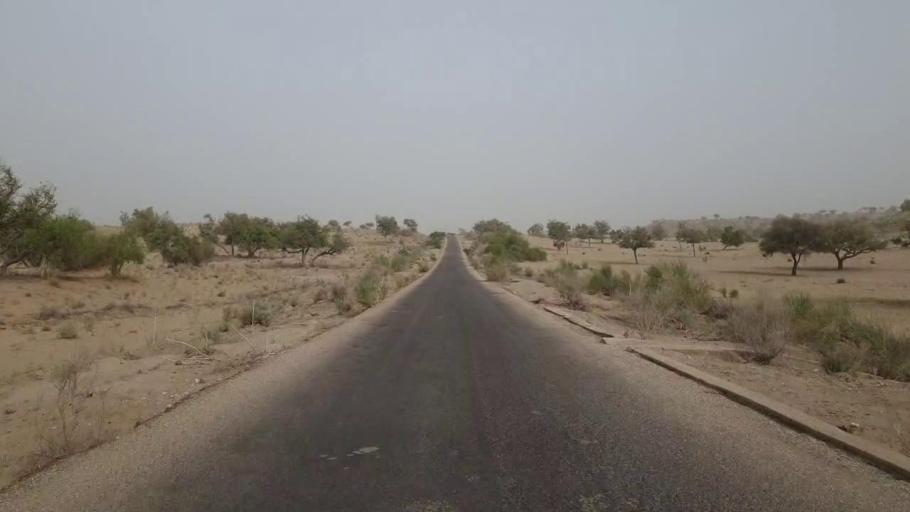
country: PK
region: Sindh
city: Islamkot
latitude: 24.5852
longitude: 70.2964
